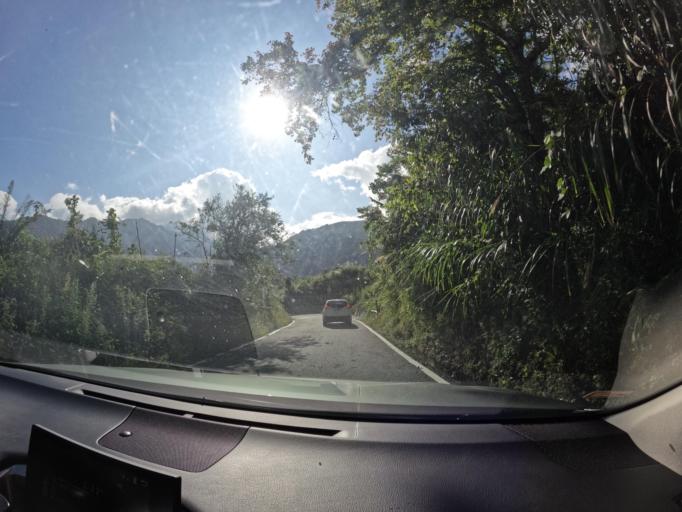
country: TW
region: Taiwan
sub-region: Taitung
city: Taitung
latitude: 23.2022
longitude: 121.0181
